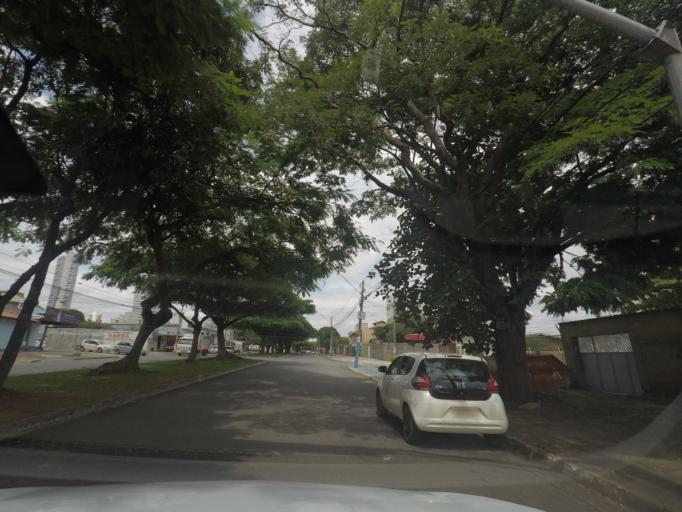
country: BR
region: Goias
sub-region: Goiania
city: Goiania
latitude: -16.6737
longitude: -49.2327
